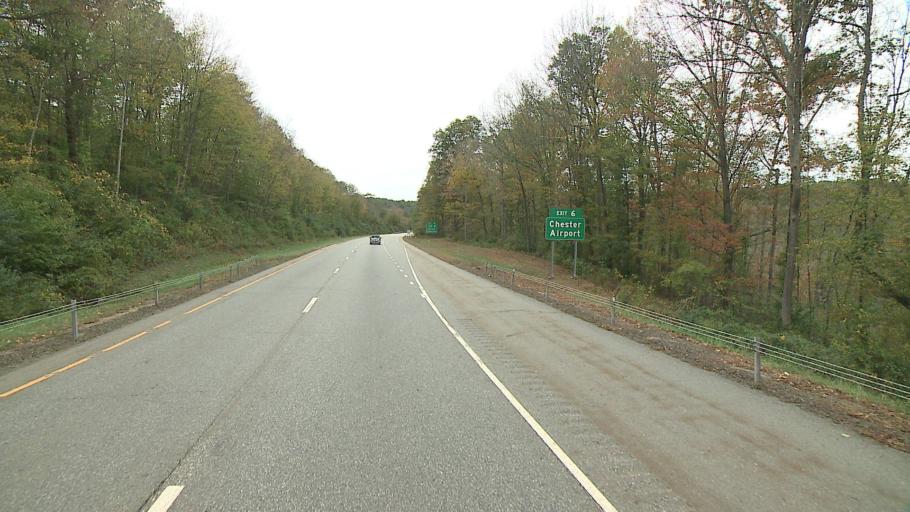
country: US
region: Connecticut
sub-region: Middlesex County
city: Chester Center
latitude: 41.3958
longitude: -72.4675
